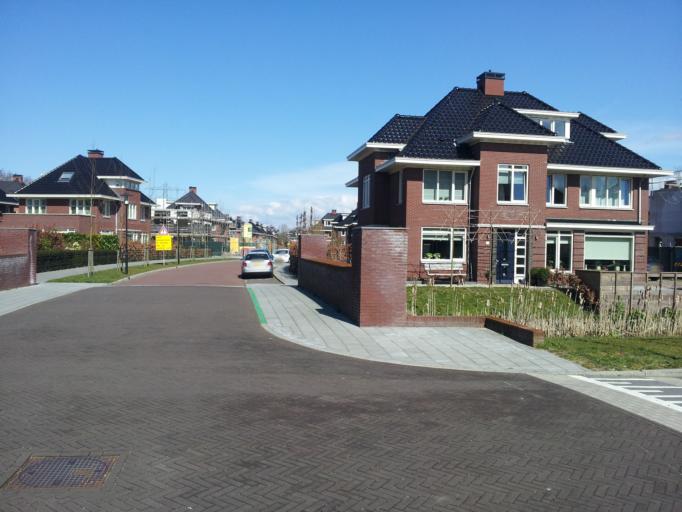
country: NL
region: South Holland
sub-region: Gemeente Voorschoten
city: Voorschoten
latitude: 52.1287
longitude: 4.4384
